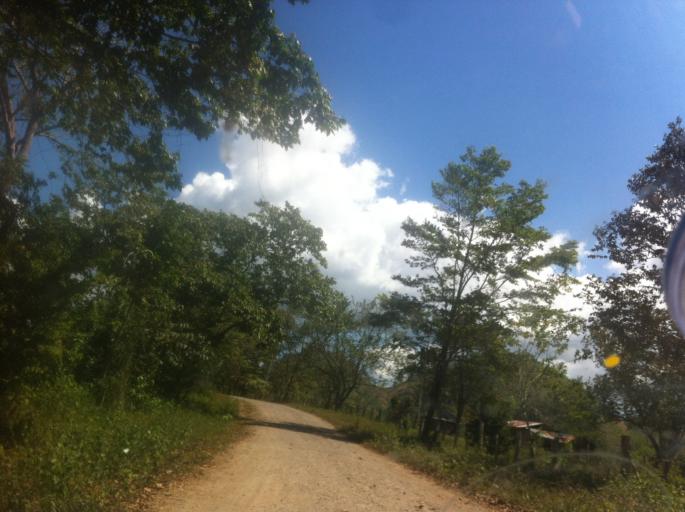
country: CR
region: Alajuela
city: Los Chiles
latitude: 11.2367
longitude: -84.5087
